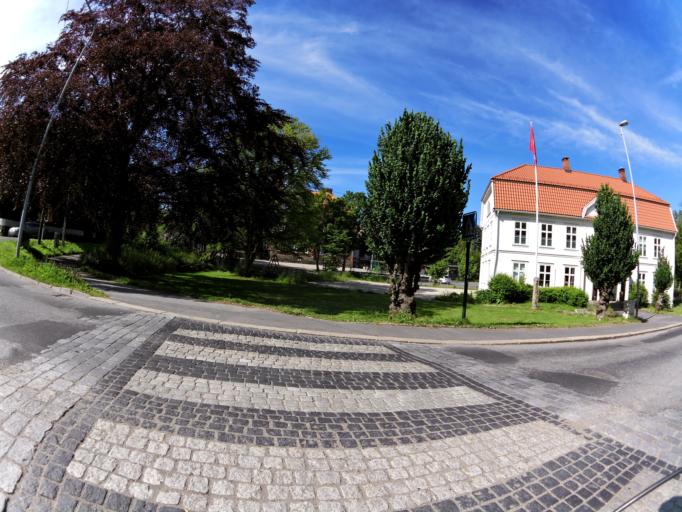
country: NO
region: Ostfold
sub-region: Fredrikstad
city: Fredrikstad
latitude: 59.2181
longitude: 10.9391
